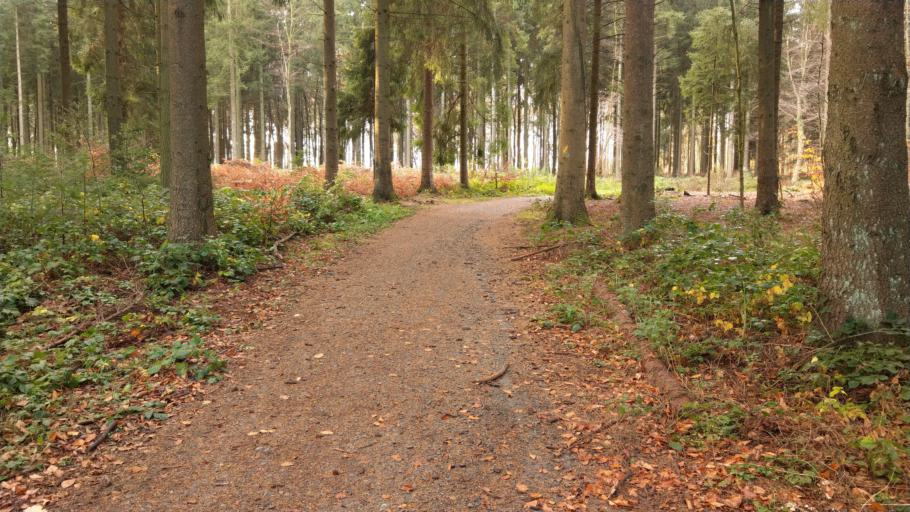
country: NL
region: Limburg
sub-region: Gemeente Vaals
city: Vaals
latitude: 50.7459
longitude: 6.0273
